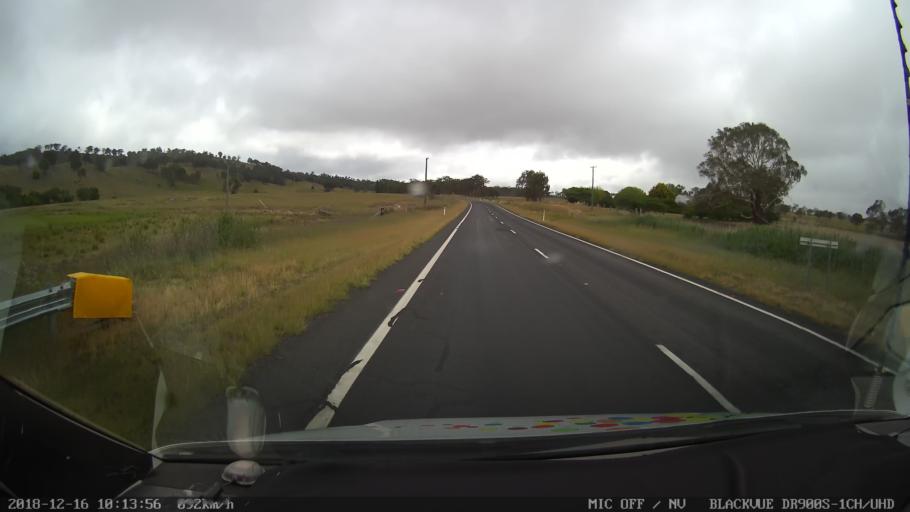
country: AU
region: New South Wales
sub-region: Tenterfield Municipality
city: Carrolls Creek
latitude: -29.2925
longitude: 151.9582
